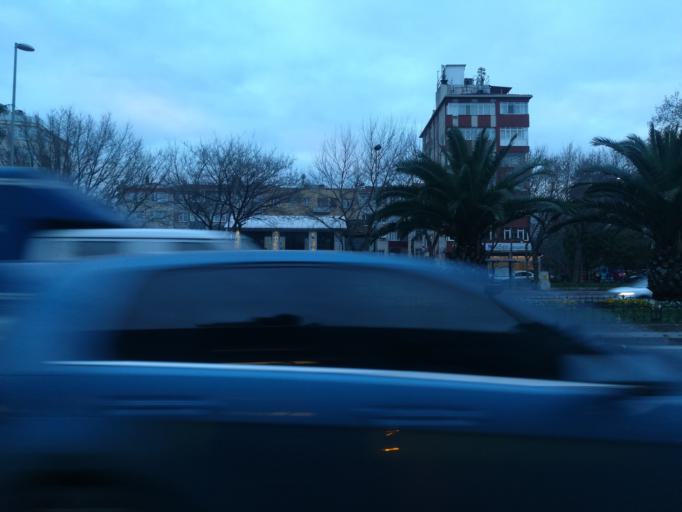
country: TR
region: Istanbul
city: Istanbul
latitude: 41.0139
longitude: 28.9449
